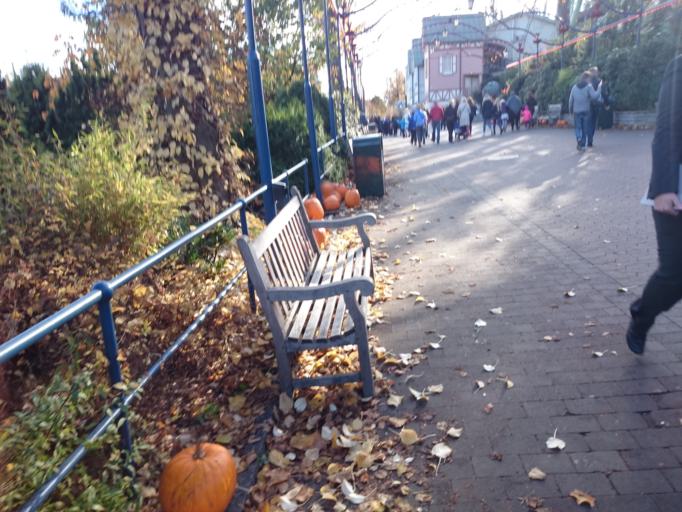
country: SE
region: Vaestra Goetaland
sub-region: Goteborg
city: Goeteborg
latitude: 57.6956
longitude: 11.9923
